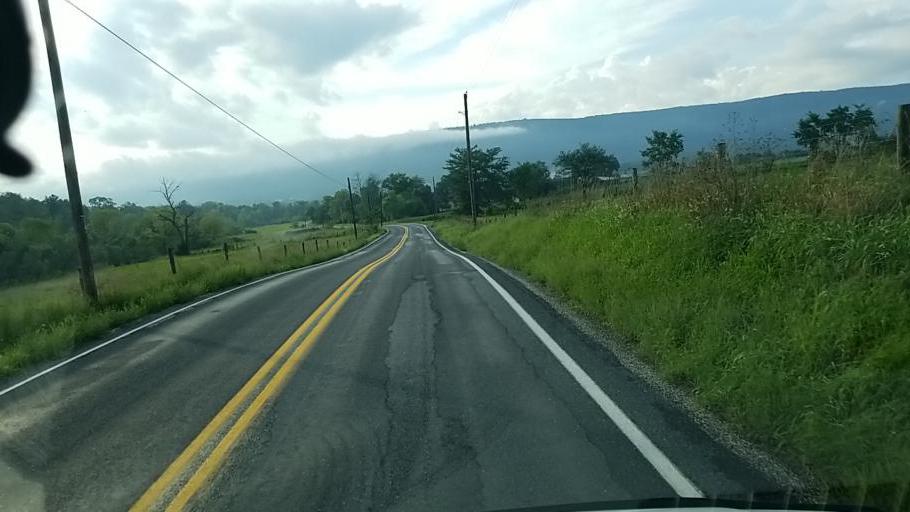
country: US
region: Pennsylvania
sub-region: Cumberland County
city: Newville
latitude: 40.1944
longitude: -77.4952
